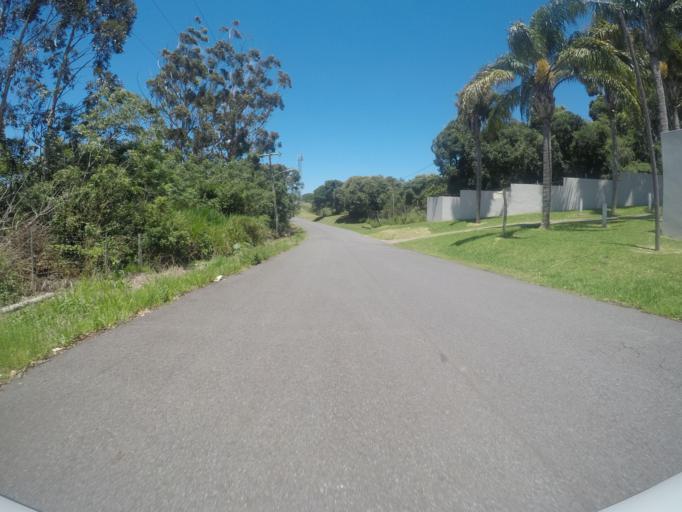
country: ZA
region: Eastern Cape
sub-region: Buffalo City Metropolitan Municipality
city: East London
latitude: -32.9346
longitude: 28.0045
